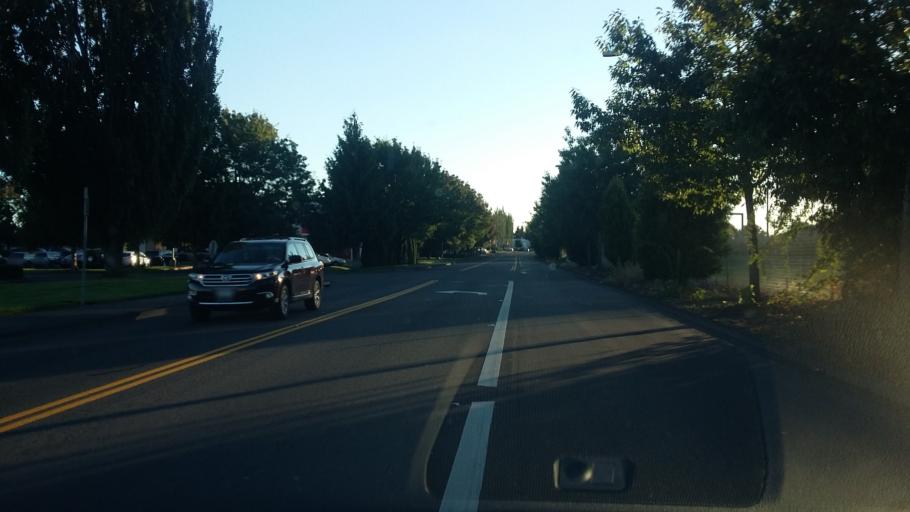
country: US
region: Washington
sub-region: Clark County
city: Walnut Grove
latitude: 45.6511
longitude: -122.5934
